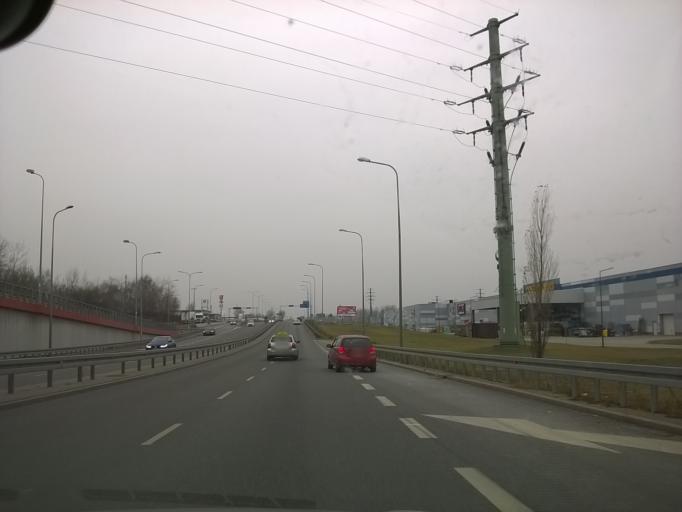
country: PL
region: Silesian Voivodeship
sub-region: Powiat gliwicki
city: Przyszowice
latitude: 50.2639
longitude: 18.7190
